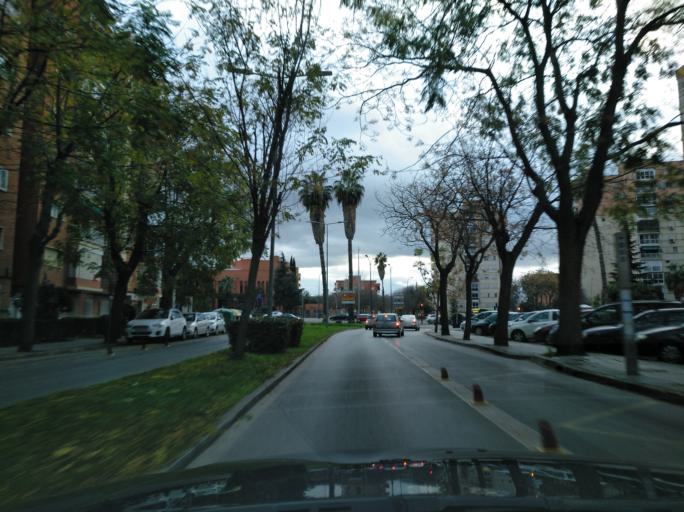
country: ES
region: Extremadura
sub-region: Provincia de Badajoz
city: Badajoz
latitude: 38.8737
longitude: -6.9801
